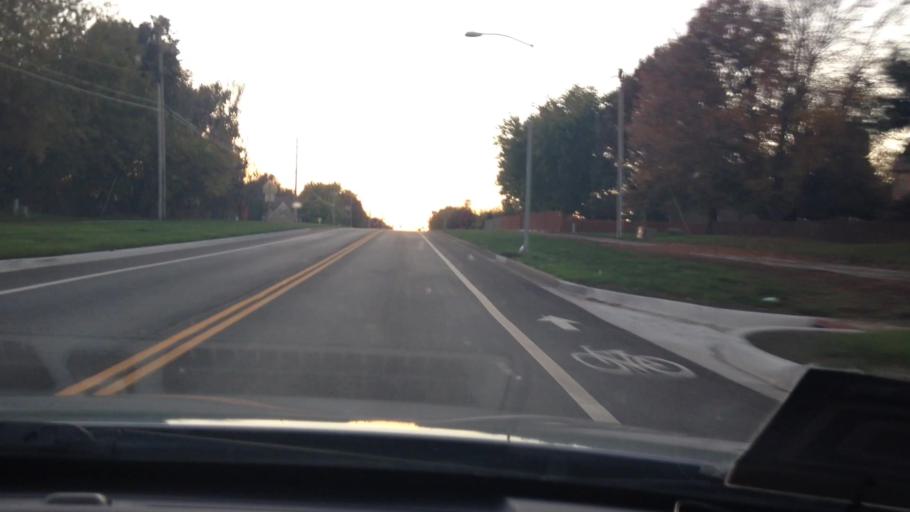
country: US
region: Kansas
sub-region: Johnson County
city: Olathe
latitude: 38.8691
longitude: -94.7548
